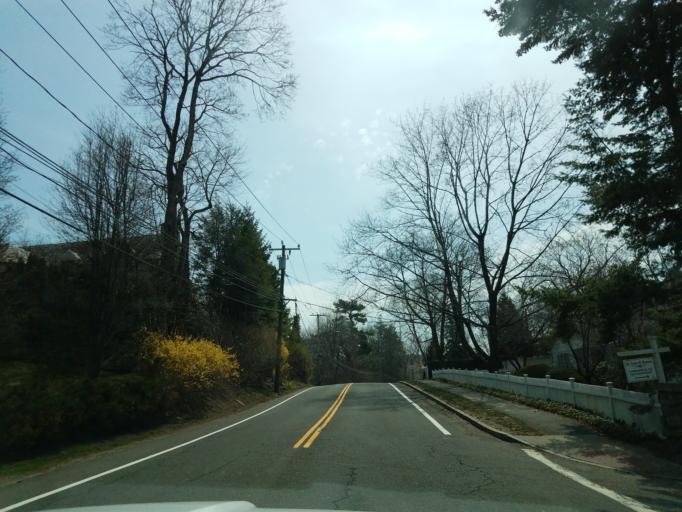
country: US
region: Connecticut
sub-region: Fairfield County
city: Greenwich
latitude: 41.0312
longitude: -73.6318
